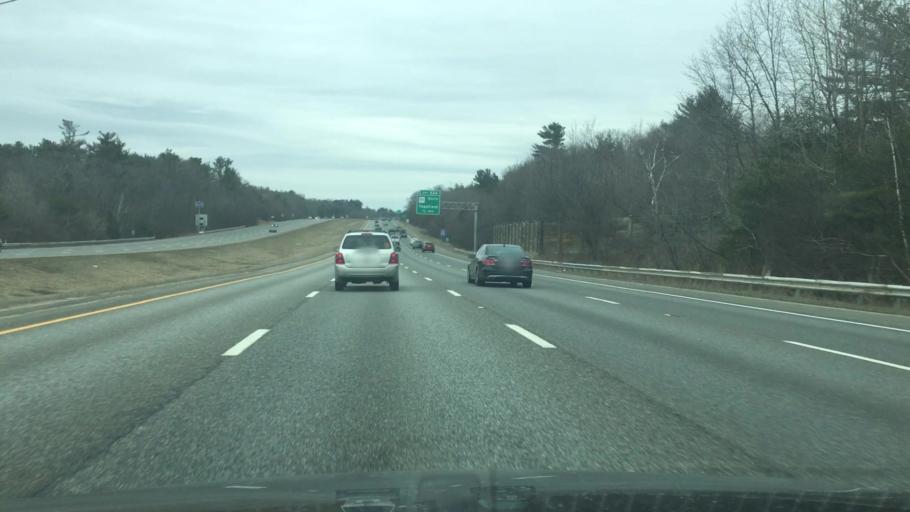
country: US
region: Massachusetts
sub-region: Essex County
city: Boxford
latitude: 42.6726
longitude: -70.9761
